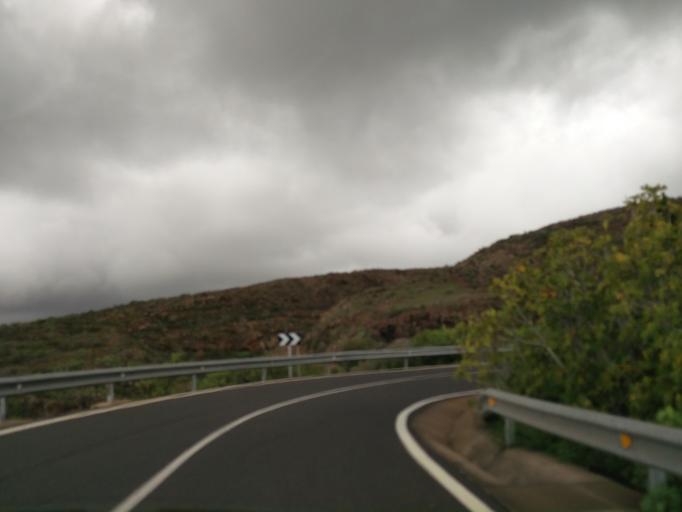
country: ES
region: Canary Islands
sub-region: Provincia de Santa Cruz de Tenerife
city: Arona
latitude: 28.1167
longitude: -16.6790
